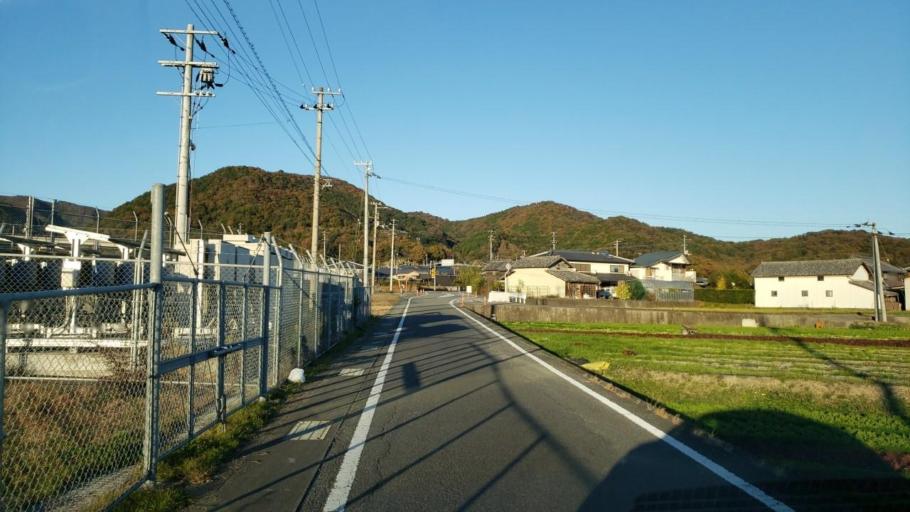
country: JP
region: Tokushima
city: Kamojimacho-jogejima
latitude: 34.0994
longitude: 134.2978
